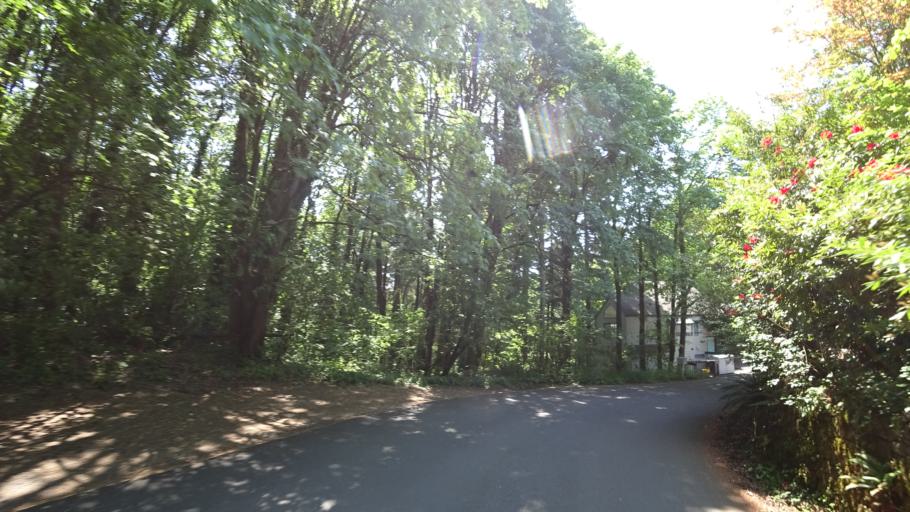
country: US
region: Oregon
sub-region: Multnomah County
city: Portland
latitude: 45.5178
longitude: -122.7108
